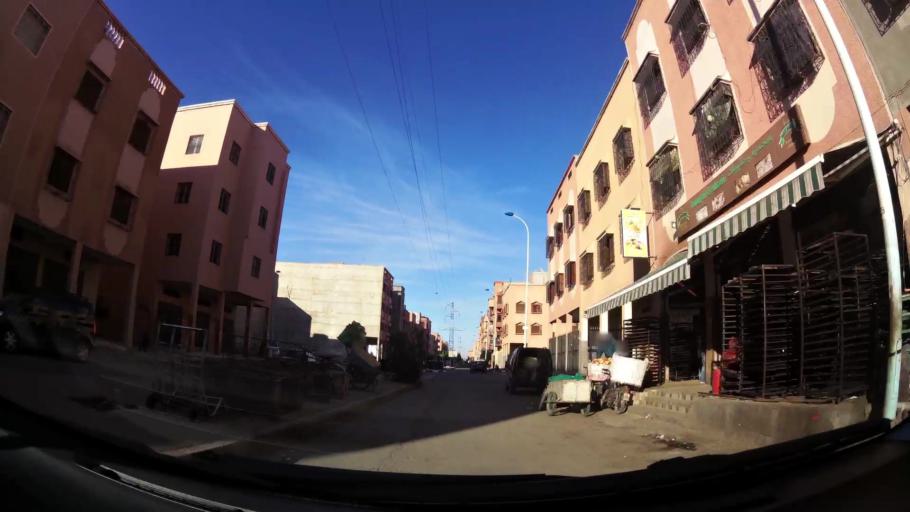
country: MA
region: Marrakech-Tensift-Al Haouz
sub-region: Marrakech
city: Marrakesh
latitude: 31.6152
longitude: -8.0620
